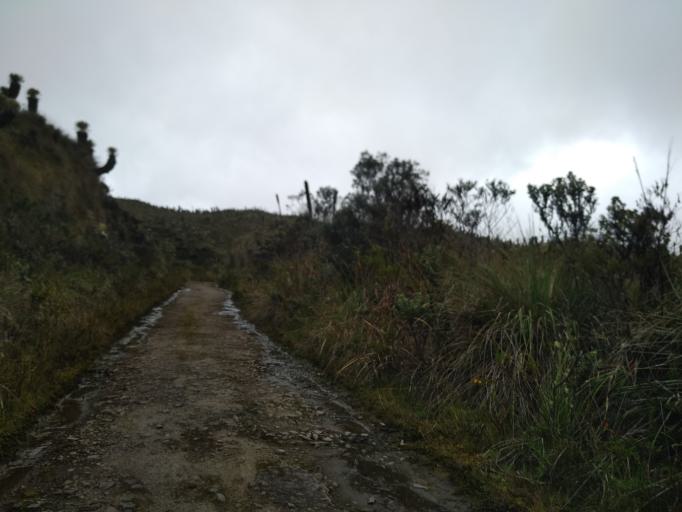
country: EC
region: Carchi
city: San Gabriel
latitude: 0.6882
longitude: -77.8502
